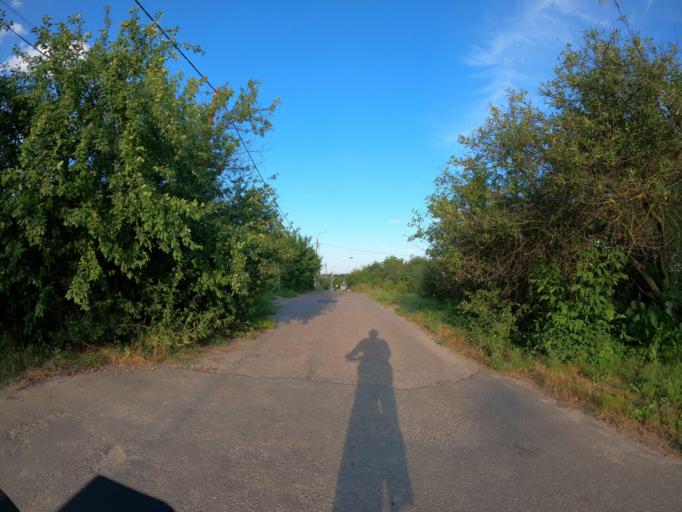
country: RU
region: Moskovskaya
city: Raduzhnyy
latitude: 55.1039
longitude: 38.7247
